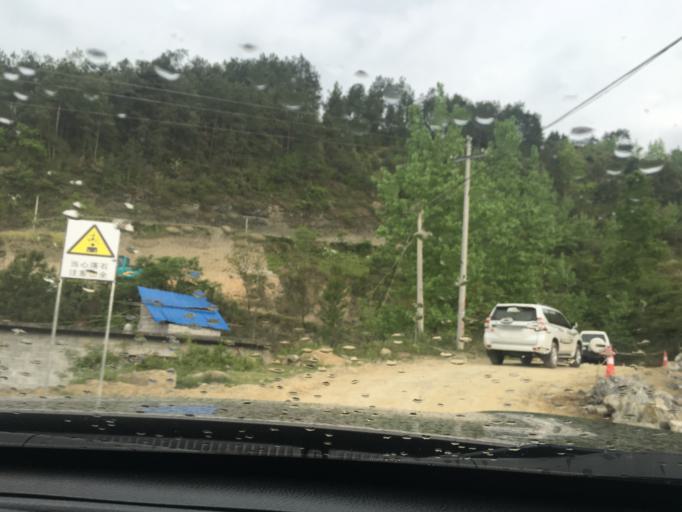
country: CN
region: Guizhou Sheng
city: Changbao
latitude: 28.2071
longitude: 108.2865
